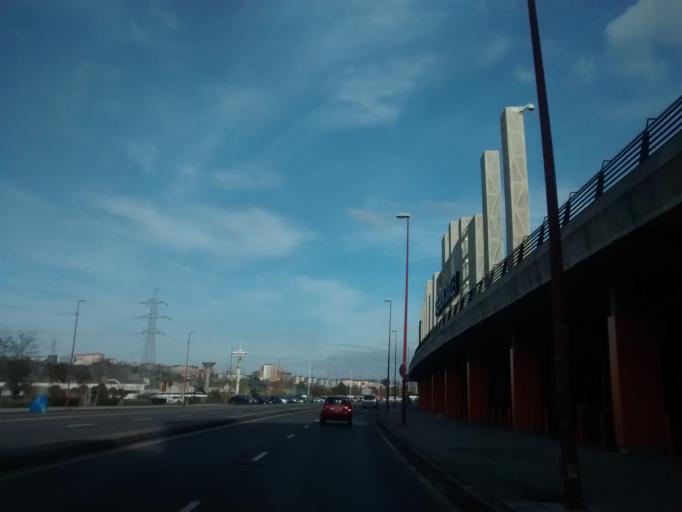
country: ES
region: Basque Country
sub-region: Bizkaia
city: Barakaldo
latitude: 43.2948
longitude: -3.0050
